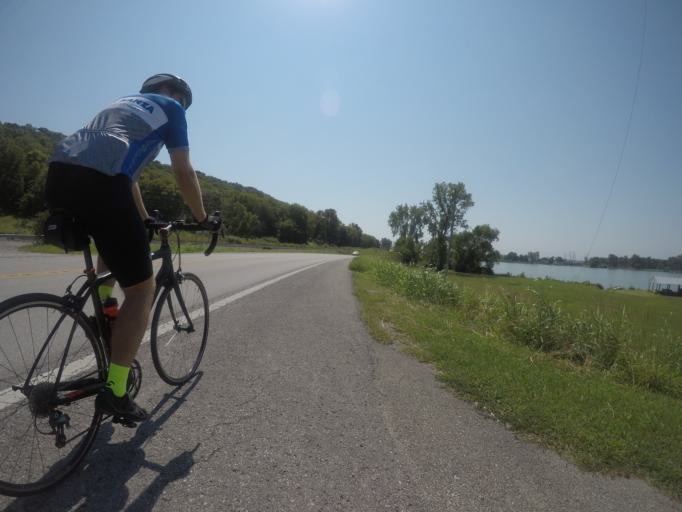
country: US
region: Kansas
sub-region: Atchison County
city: Atchison
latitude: 39.5487
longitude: -95.0456
